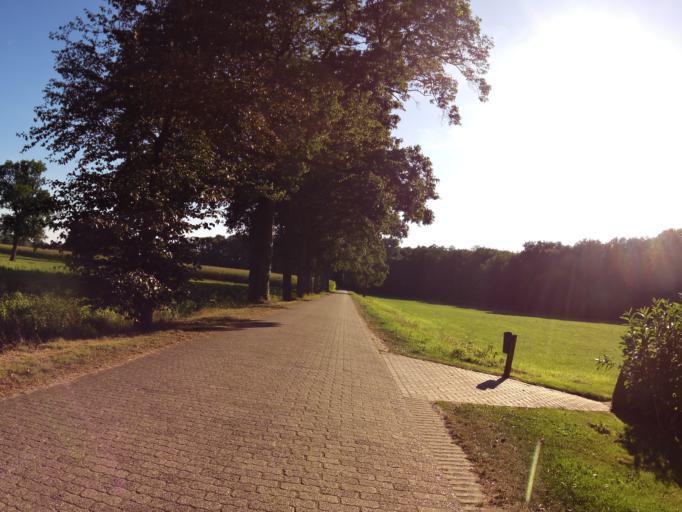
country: NL
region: Gelderland
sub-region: Gemeente Winterswijk
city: Winterswijk
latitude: 51.9558
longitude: 6.7560
